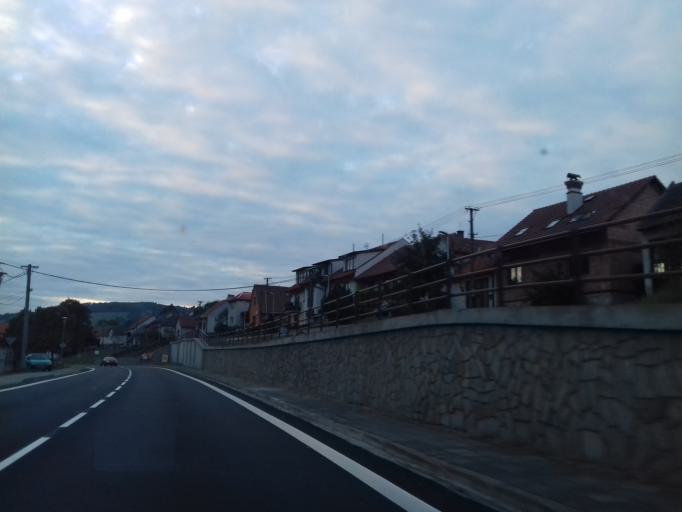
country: CZ
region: Zlin
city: Bojkovice
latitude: 48.9644
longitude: 17.8692
